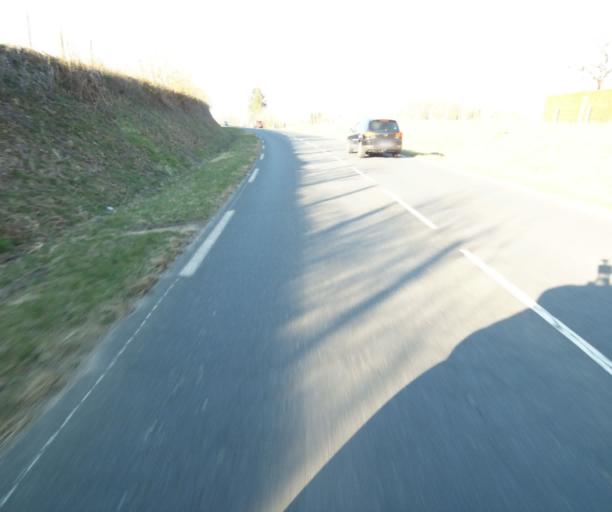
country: FR
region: Limousin
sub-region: Departement de la Correze
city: Saint-Clement
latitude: 45.3466
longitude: 1.6953
